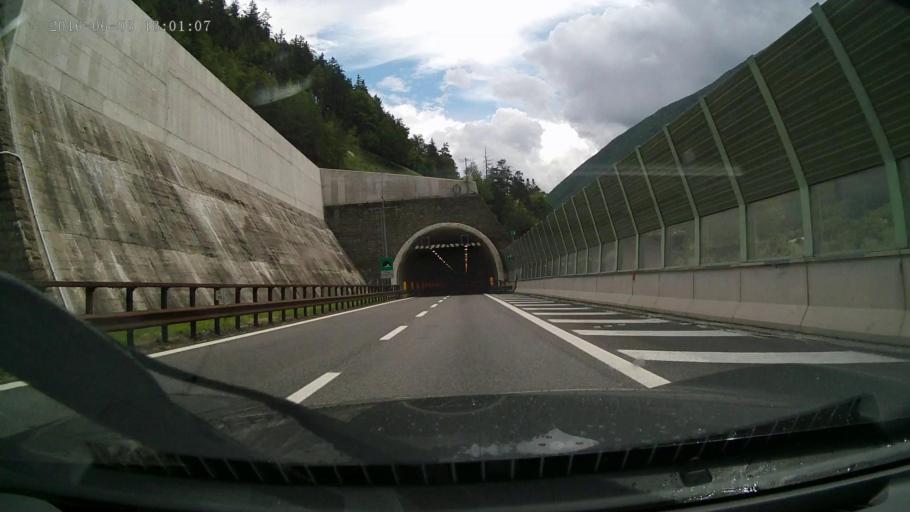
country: IT
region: Trentino-Alto Adige
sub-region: Bolzano
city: Fortezza
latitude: 46.7919
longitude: 11.6108
